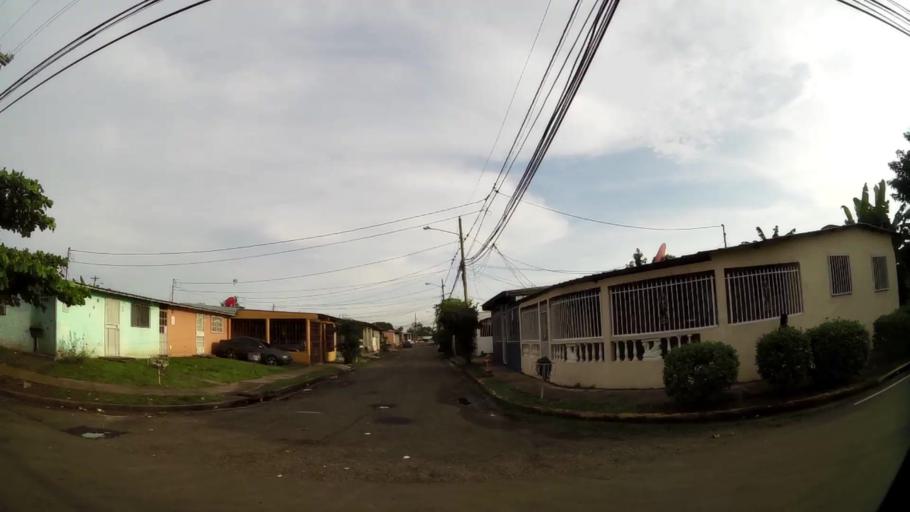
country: PA
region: Panama
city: Tocumen
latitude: 9.0798
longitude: -79.3613
